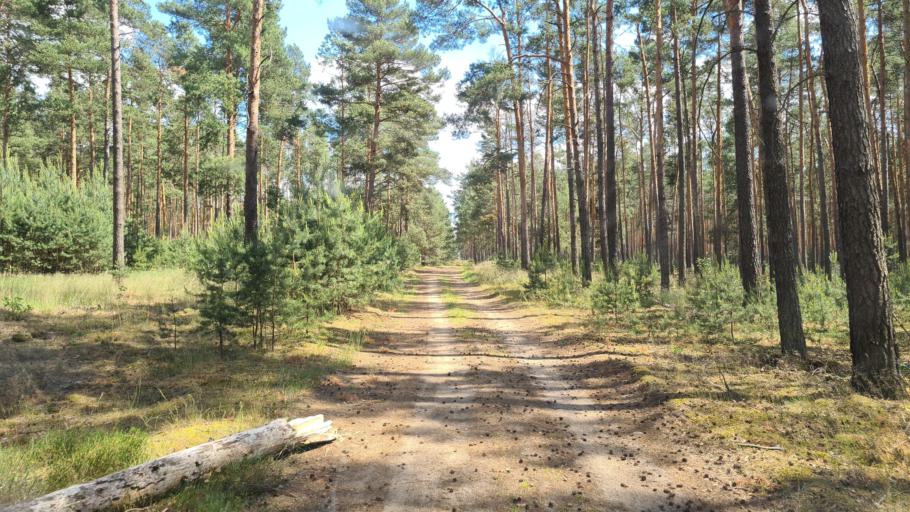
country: DE
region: Brandenburg
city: Crinitz
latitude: 51.6601
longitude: 13.7984
